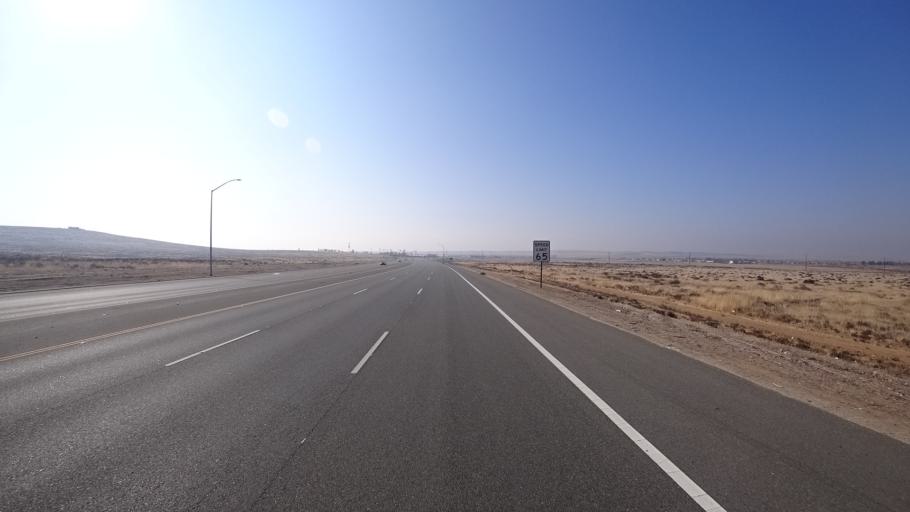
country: US
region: California
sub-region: Kern County
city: Oildale
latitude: 35.4028
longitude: -118.8731
